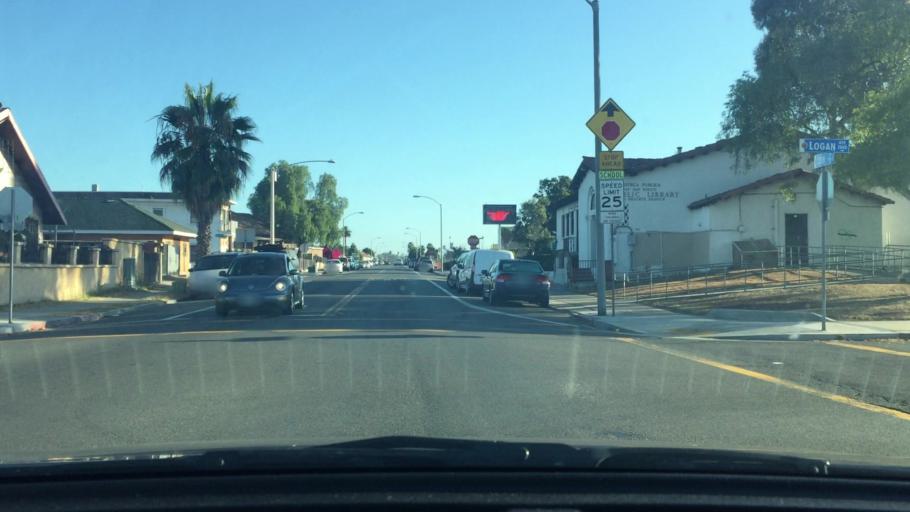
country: US
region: California
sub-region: San Diego County
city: San Diego
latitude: 32.6969
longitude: -117.1338
